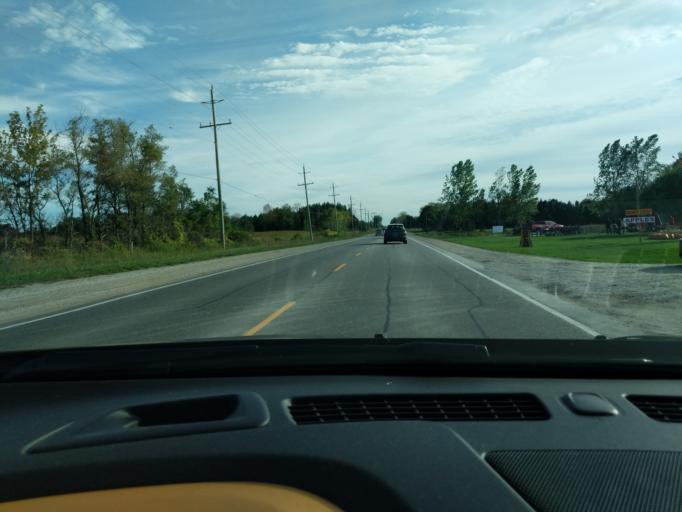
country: CA
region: Ontario
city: Wasaga Beach
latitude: 44.4402
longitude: -80.1009
